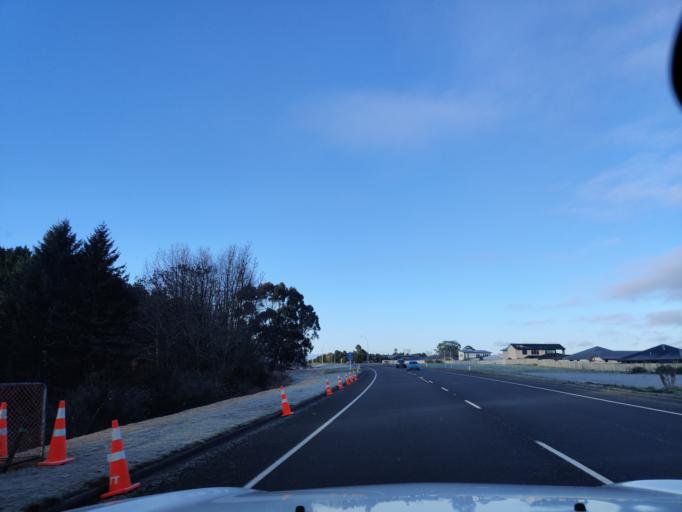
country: NZ
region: Waikato
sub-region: Taupo District
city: Taupo
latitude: -38.7341
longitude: 176.0721
